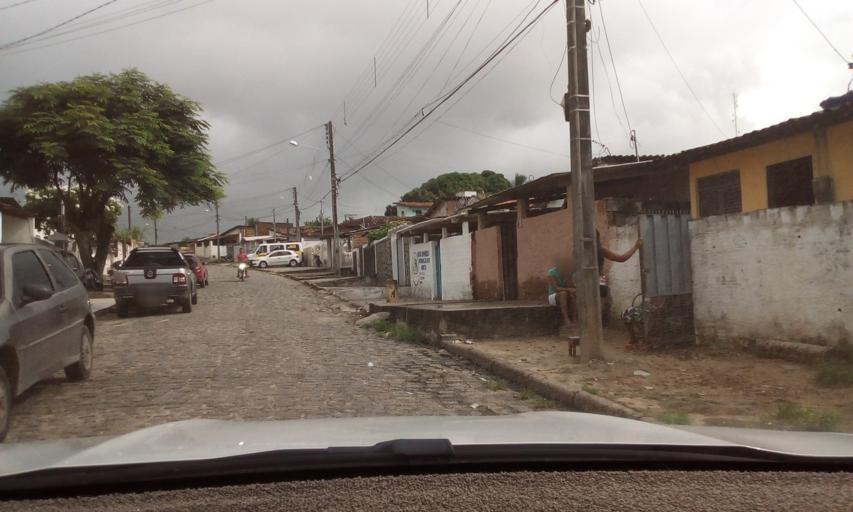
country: BR
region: Paraiba
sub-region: Bayeux
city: Bayeux
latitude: -7.1544
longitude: -34.9027
